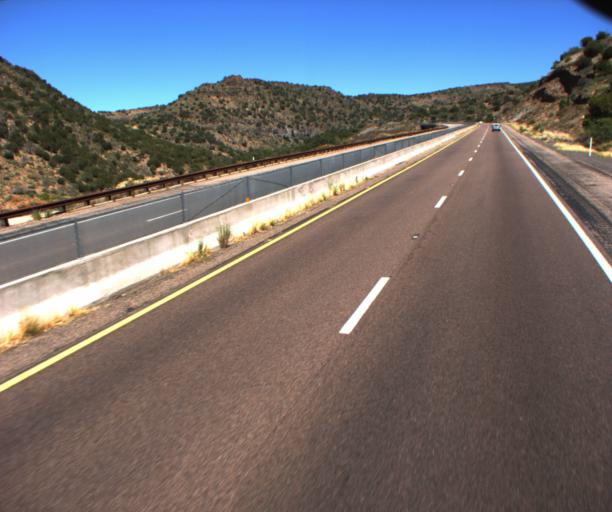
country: US
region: Arizona
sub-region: Gila County
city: Tonto Basin
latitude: 33.8889
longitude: -111.4526
